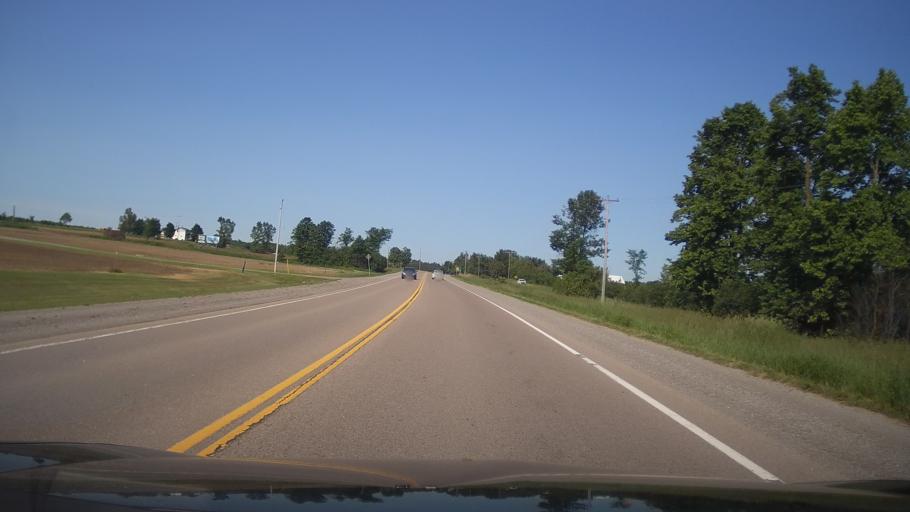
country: CA
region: Ontario
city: Omemee
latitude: 44.3485
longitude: -78.7903
